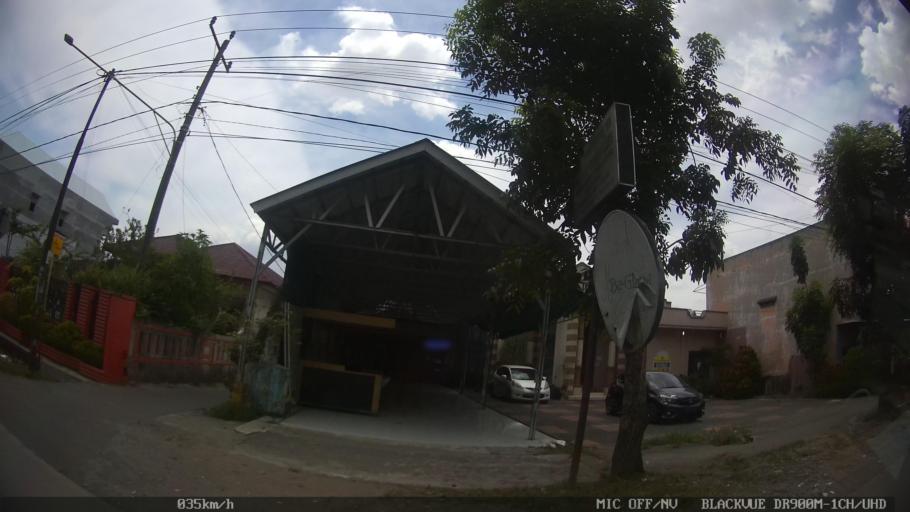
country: ID
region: North Sumatra
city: Binjai
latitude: 3.6252
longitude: 98.5062
